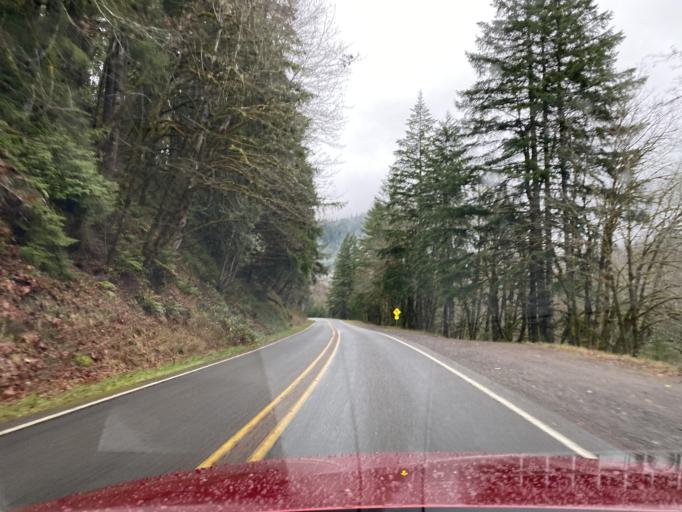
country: US
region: Oregon
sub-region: Lane County
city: Oakridge
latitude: 43.7527
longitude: -122.5260
